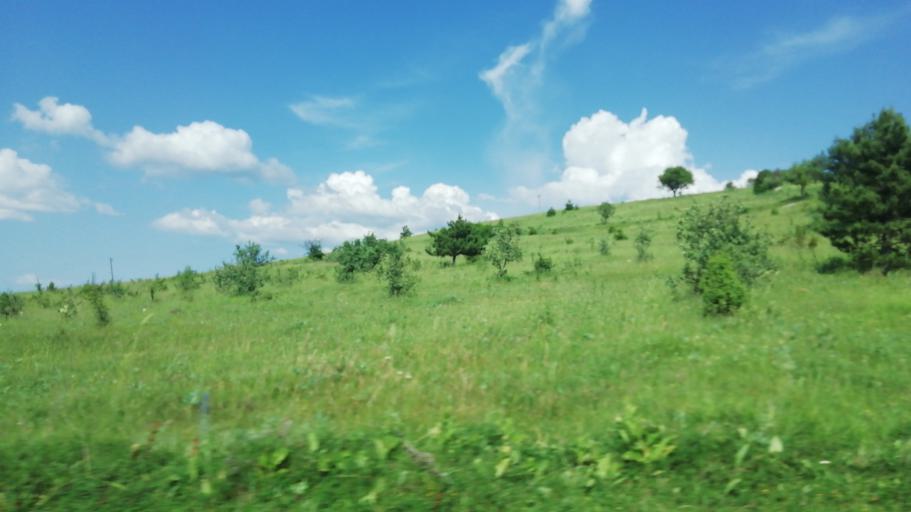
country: TR
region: Karabuk
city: Karabuk
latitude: 41.1270
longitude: 32.5757
